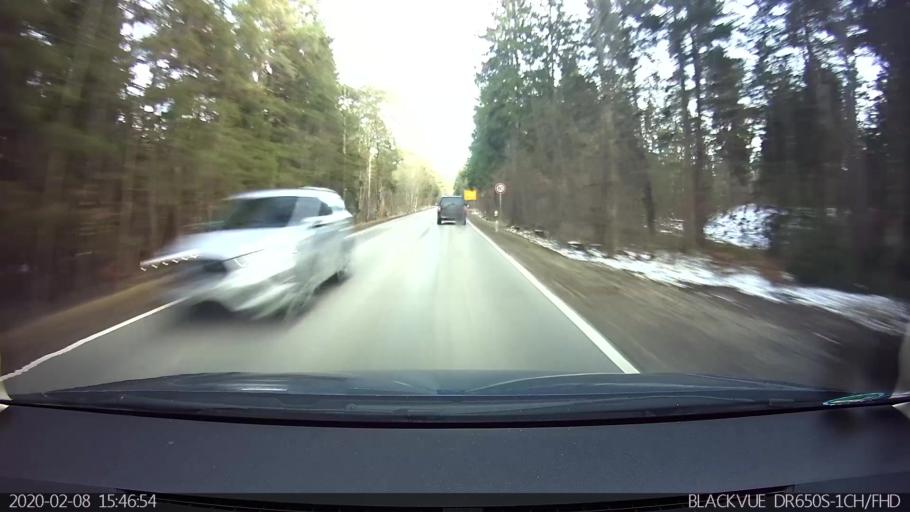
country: DE
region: Bavaria
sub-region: Upper Bavaria
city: Geretsried
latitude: 47.8586
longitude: 11.5010
